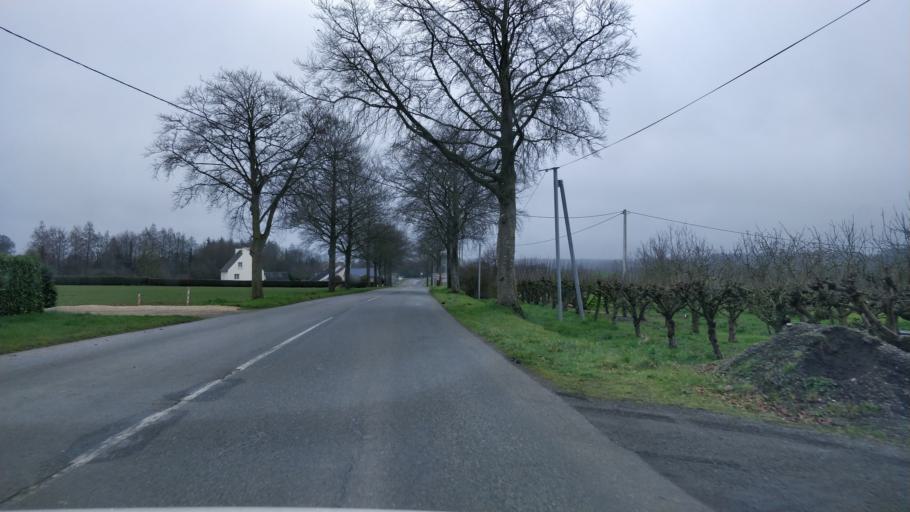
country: FR
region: Brittany
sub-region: Departement des Cotes-d'Armor
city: Broons
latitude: 48.3099
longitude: -2.2411
